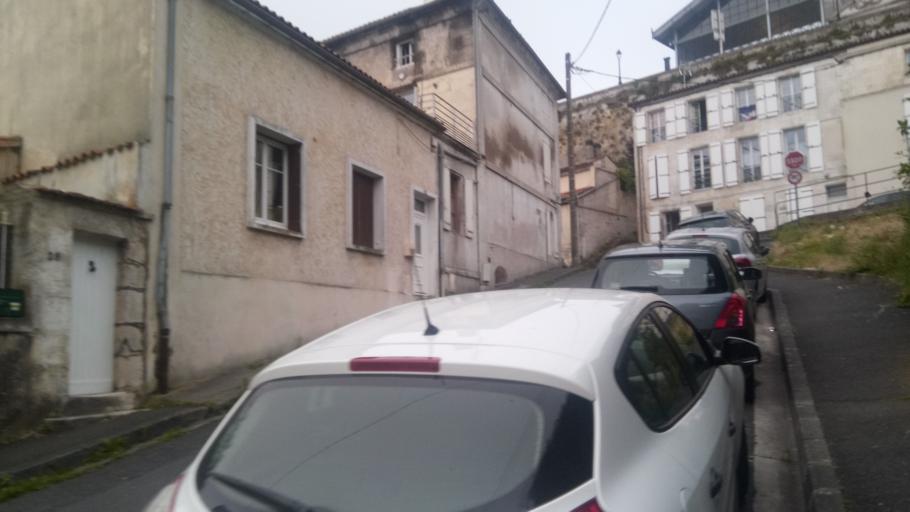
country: FR
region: Poitou-Charentes
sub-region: Departement de la Charente
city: Angouleme
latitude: 45.6504
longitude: 0.1584
